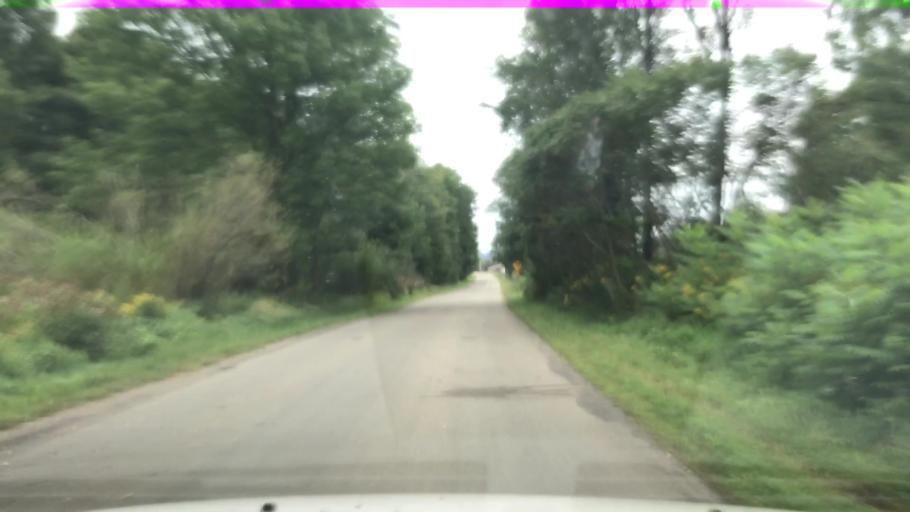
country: US
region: New York
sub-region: Cattaraugus County
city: Little Valley
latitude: 42.3287
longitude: -78.7093
